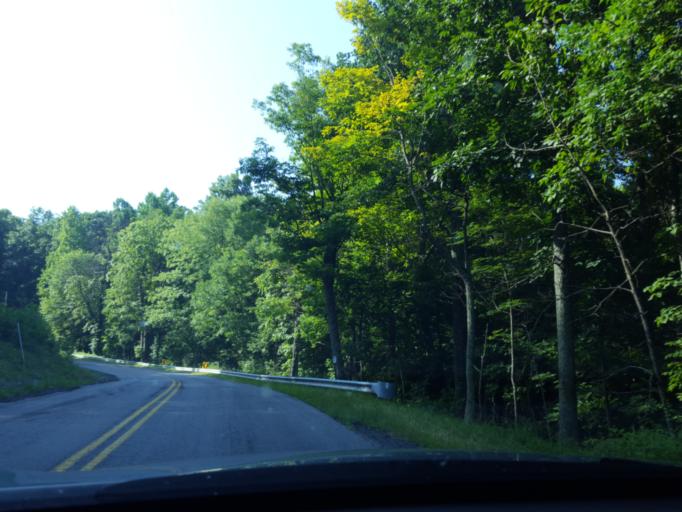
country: US
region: Virginia
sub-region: Nelson County
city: Nellysford
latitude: 37.9030
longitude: -78.9911
